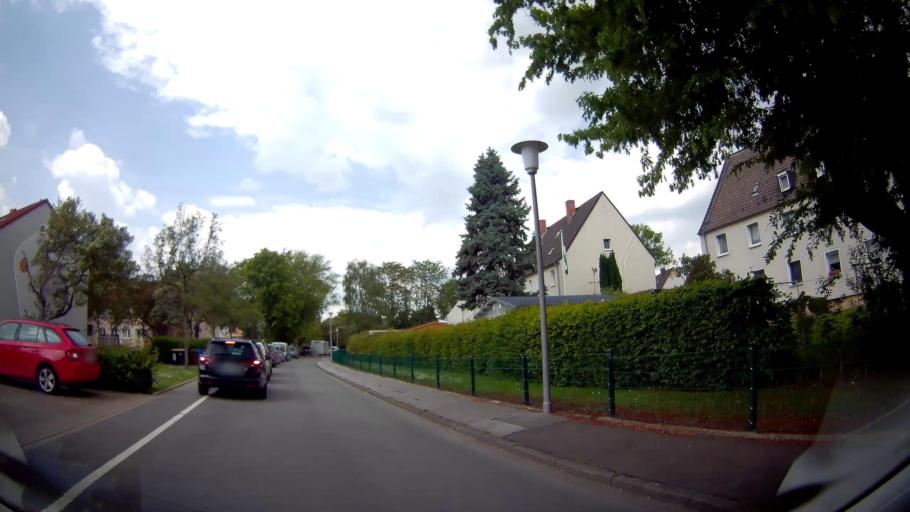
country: DE
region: North Rhine-Westphalia
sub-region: Regierungsbezirk Munster
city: Gladbeck
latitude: 51.5457
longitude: 7.0227
